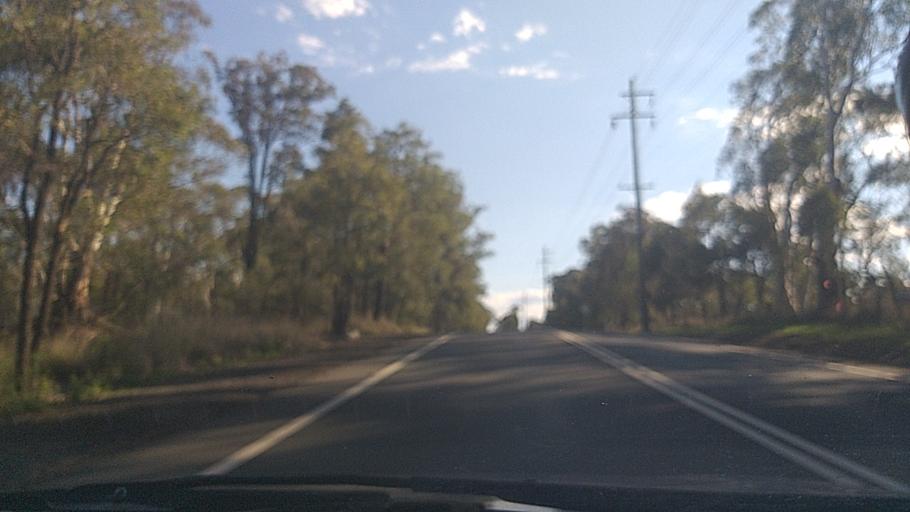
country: AU
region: New South Wales
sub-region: Hawkesbury
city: South Windsor
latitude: -33.6517
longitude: 150.7749
